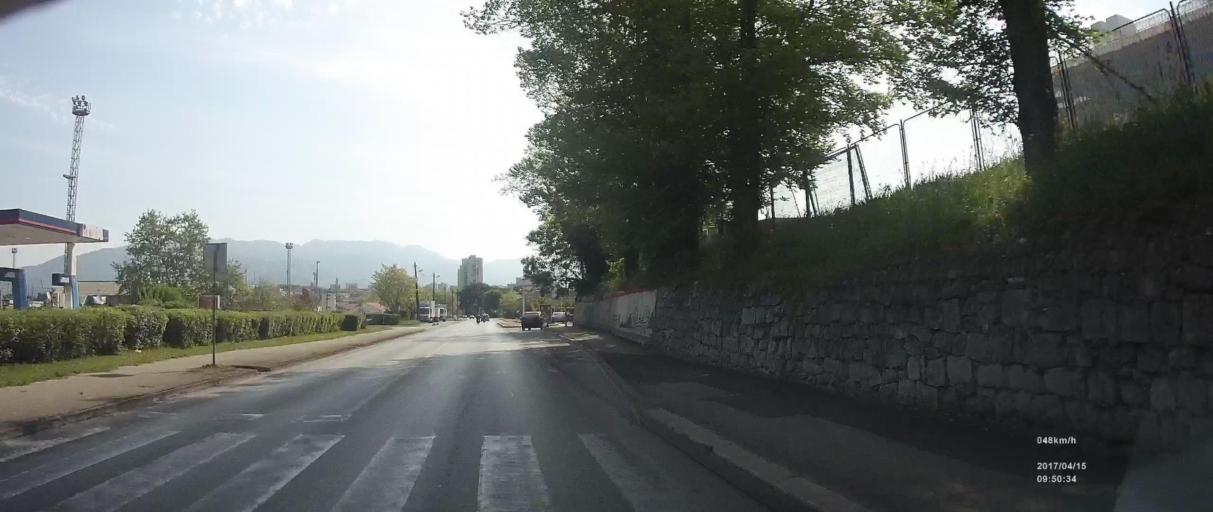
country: HR
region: Splitsko-Dalmatinska
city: Vranjic
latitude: 43.5214
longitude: 16.4536
